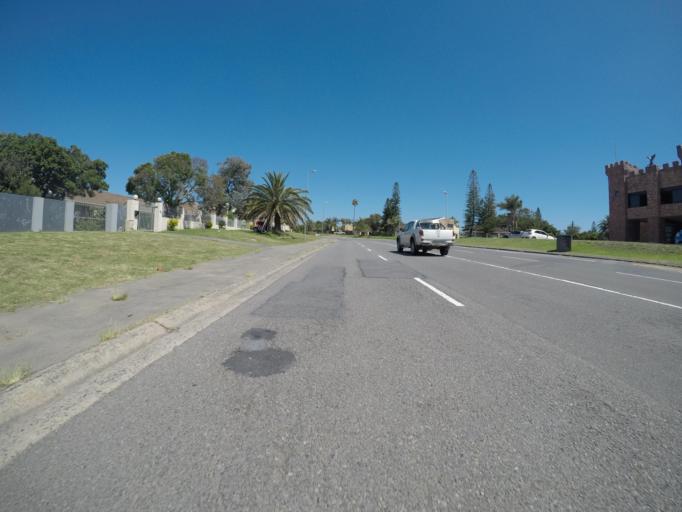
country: ZA
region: Eastern Cape
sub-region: Buffalo City Metropolitan Municipality
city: East London
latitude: -32.9674
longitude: 27.9464
